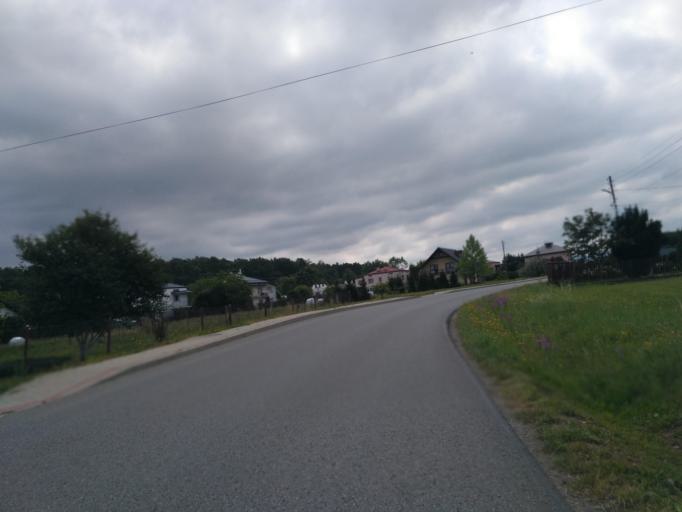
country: PL
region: Subcarpathian Voivodeship
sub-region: Powiat krosnienski
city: Kroscienko Wyzne
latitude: 49.6452
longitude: 21.8224
